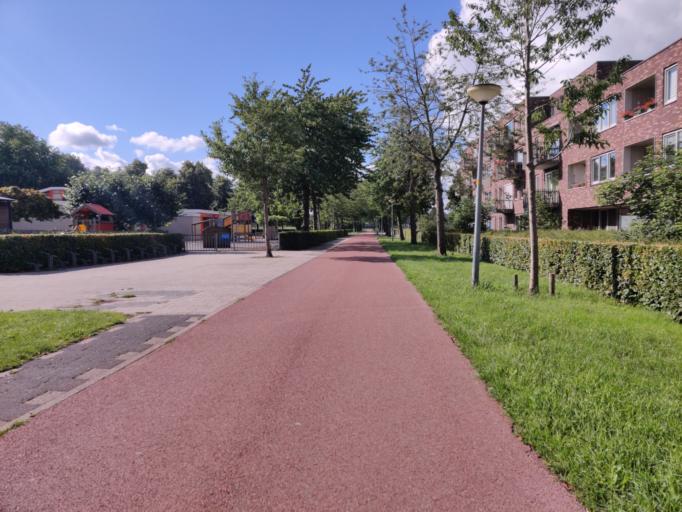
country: NL
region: Flevoland
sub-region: Gemeente Zeewolde
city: Zeewolde
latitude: 52.3322
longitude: 5.5360
